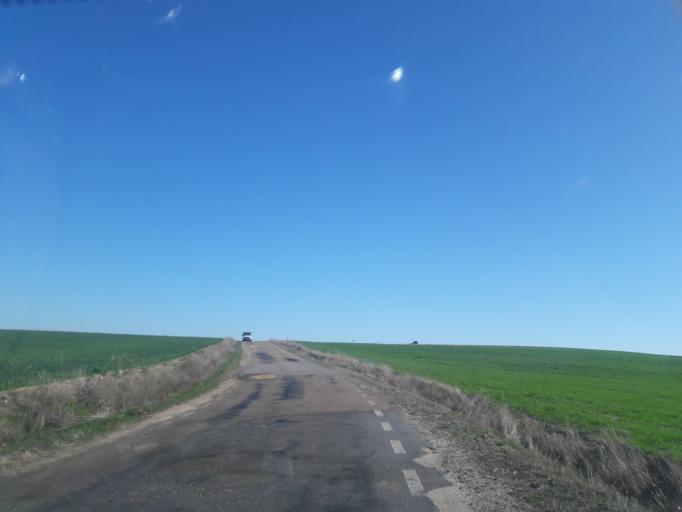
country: ES
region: Castille and Leon
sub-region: Provincia de Salamanca
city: Tordillos
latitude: 40.8745
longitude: -5.3295
